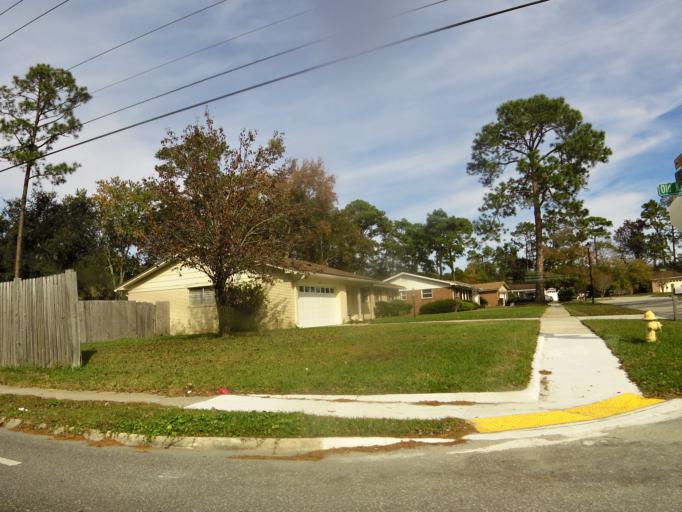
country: US
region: Florida
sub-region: Duval County
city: Jacksonville
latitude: 30.2274
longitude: -81.5956
